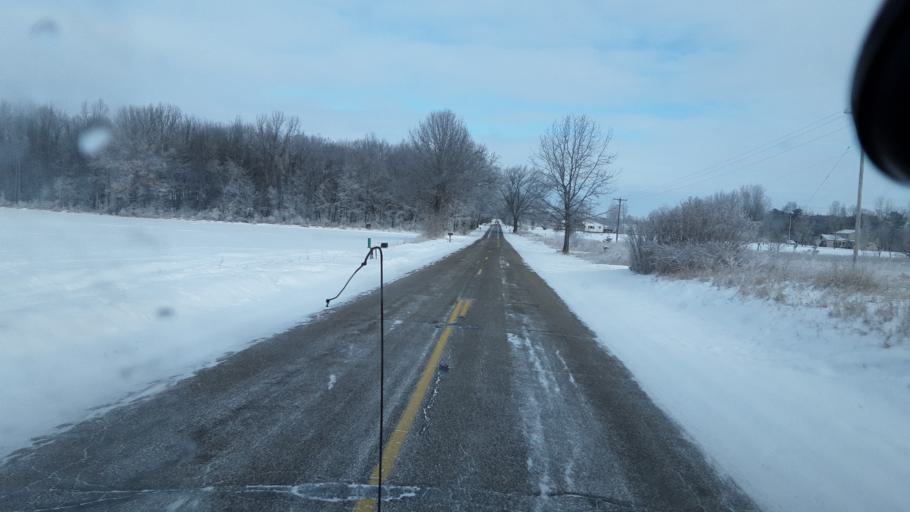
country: US
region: Michigan
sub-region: Ingham County
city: Leslie
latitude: 42.3755
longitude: -84.4924
